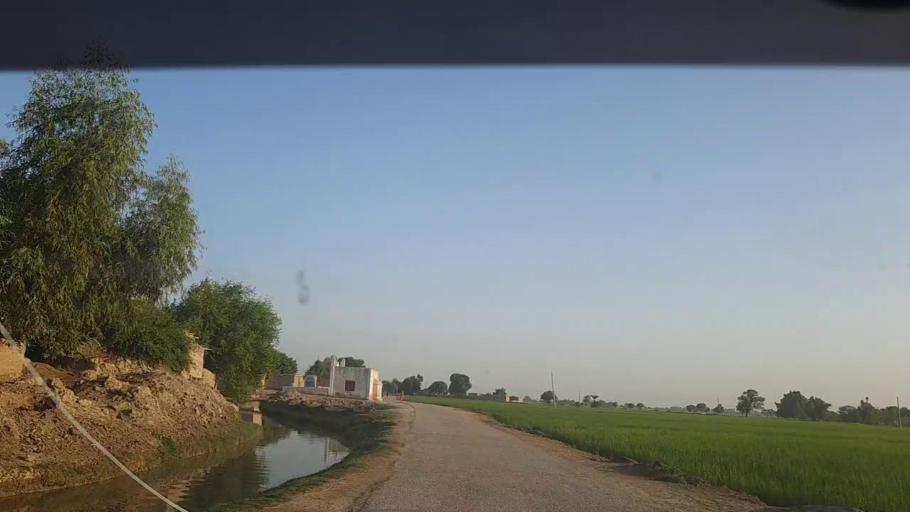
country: PK
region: Sindh
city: Rustam jo Goth
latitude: 28.1148
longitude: 68.8988
